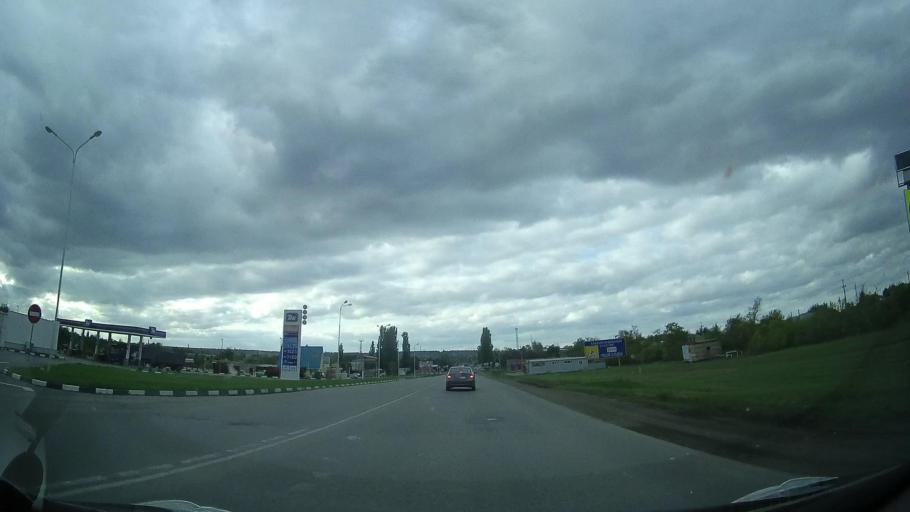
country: RU
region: Rostov
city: Kagal'nitskaya
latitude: 46.8765
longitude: 40.1583
